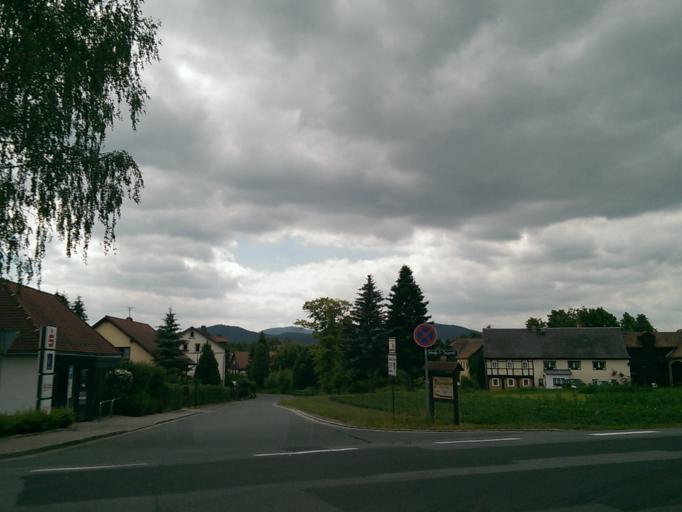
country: DE
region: Saxony
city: Bertsdorf-Hoernitz
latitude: 50.9006
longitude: 14.7486
